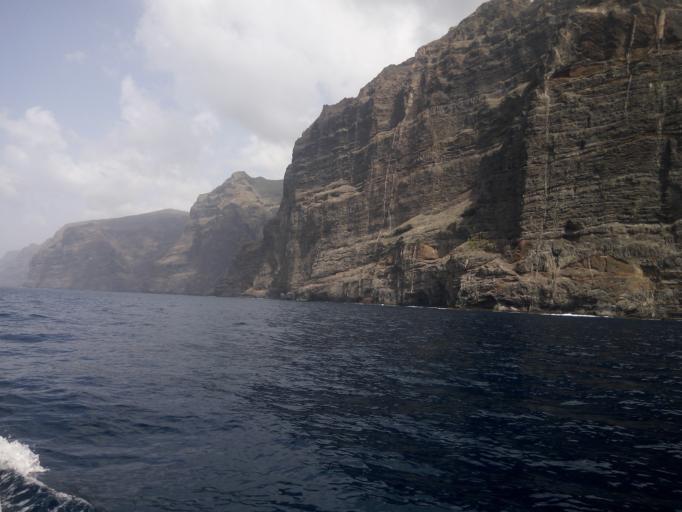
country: ES
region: Canary Islands
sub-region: Provincia de Santa Cruz de Tenerife
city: Santiago del Teide
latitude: 28.2703
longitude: -16.8607
